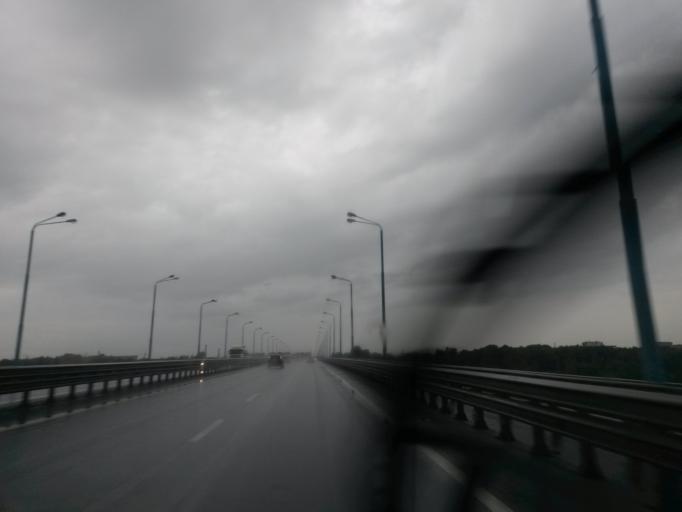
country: RU
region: Jaroslavl
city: Yaroslavl
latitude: 57.6749
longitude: 39.8569
